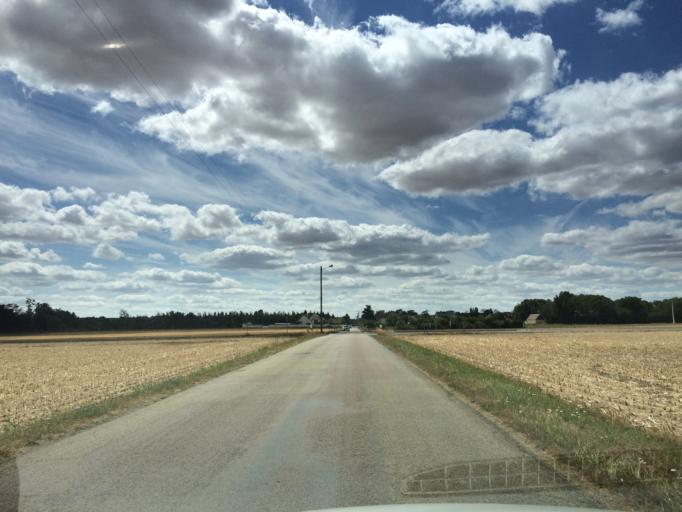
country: FR
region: Bourgogne
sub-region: Departement de l'Yonne
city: Laroche-Saint-Cydroine
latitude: 47.9548
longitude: 3.4949
